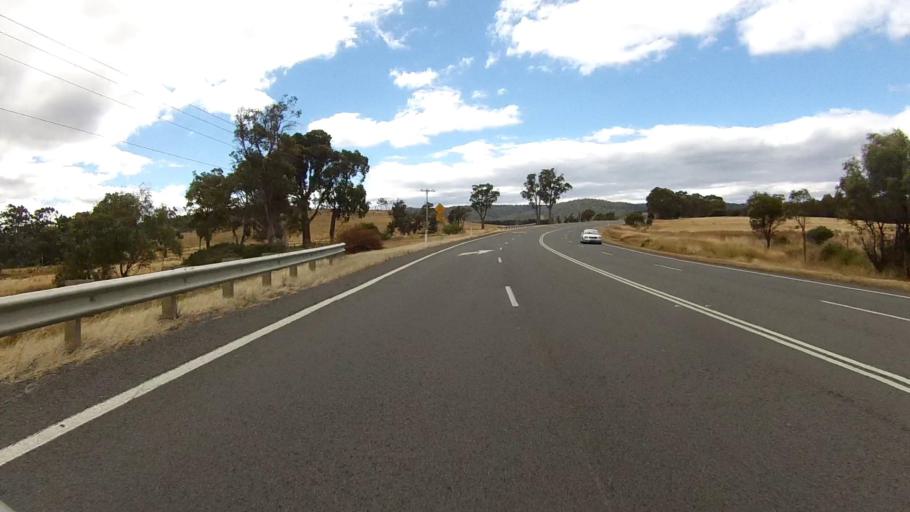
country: AU
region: Tasmania
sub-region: Sorell
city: Sorell
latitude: -42.6408
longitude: 147.5800
